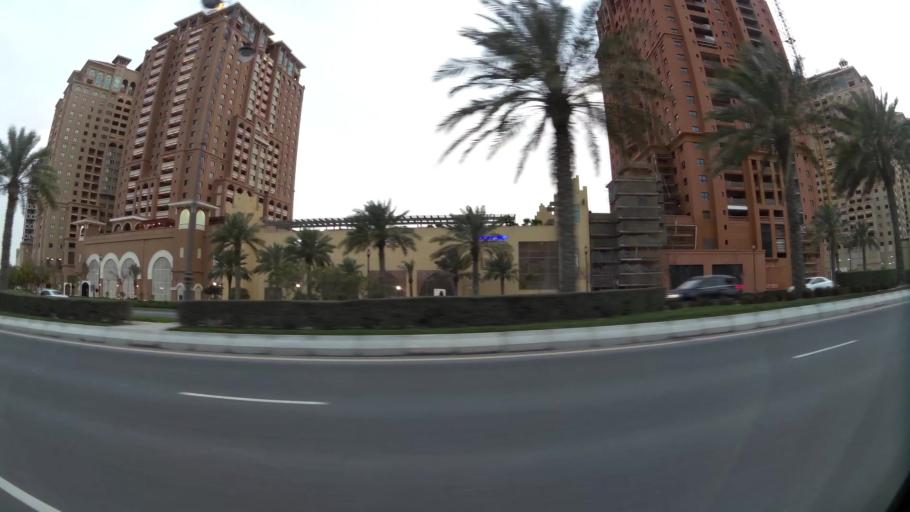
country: QA
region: Baladiyat ad Dawhah
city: Doha
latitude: 25.3730
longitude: 51.5488
